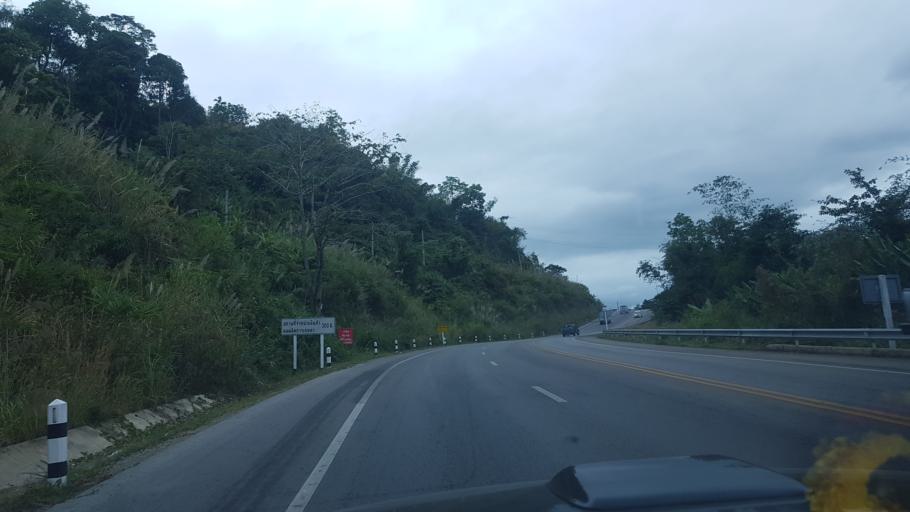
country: TH
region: Phetchabun
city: Khao Kho
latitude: 16.5555
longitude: 101.0274
